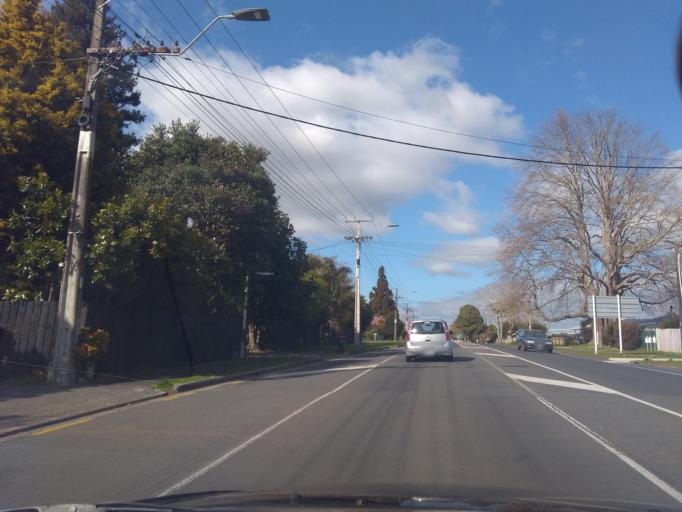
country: NZ
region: Northland
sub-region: Whangarei
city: Whangarei
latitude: -35.6872
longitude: 174.3270
